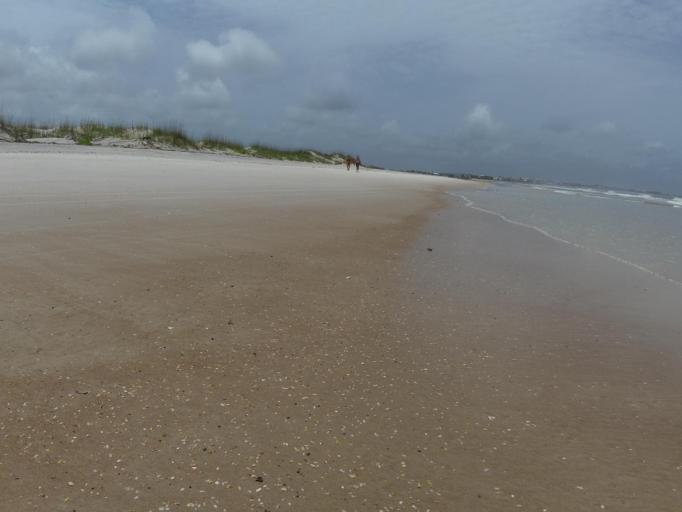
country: US
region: Florida
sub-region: Saint Johns County
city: Saint Augustine
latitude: 29.9059
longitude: -81.2790
